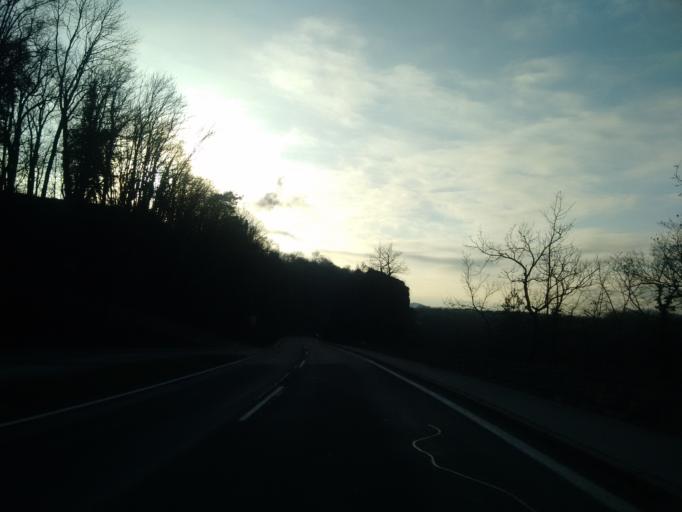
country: AT
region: Lower Austria
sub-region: Politischer Bezirk Melk
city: Emmersdorf an der Donau
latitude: 48.2335
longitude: 15.3417
